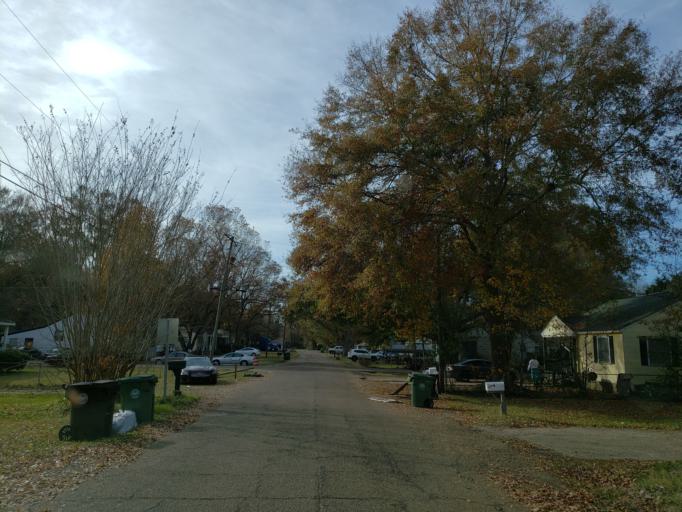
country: US
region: Mississippi
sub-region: Forrest County
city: Hattiesburg
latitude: 31.3340
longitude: -89.3174
